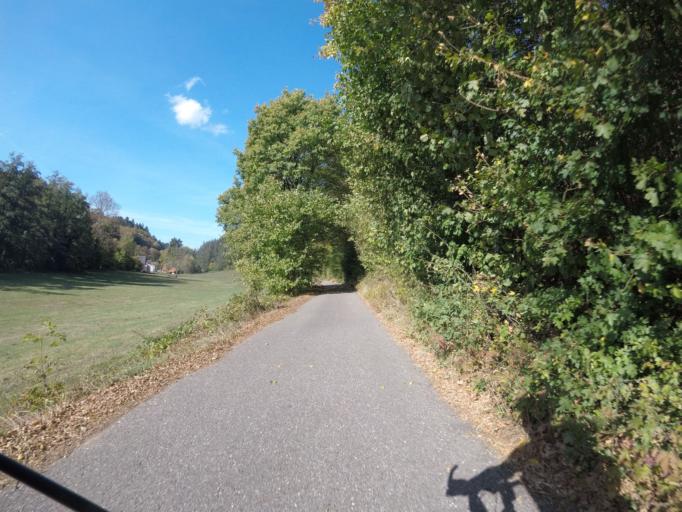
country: DE
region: Baden-Wuerttemberg
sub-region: Karlsruhe Region
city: Knittlingen
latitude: 48.9986
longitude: 8.7373
